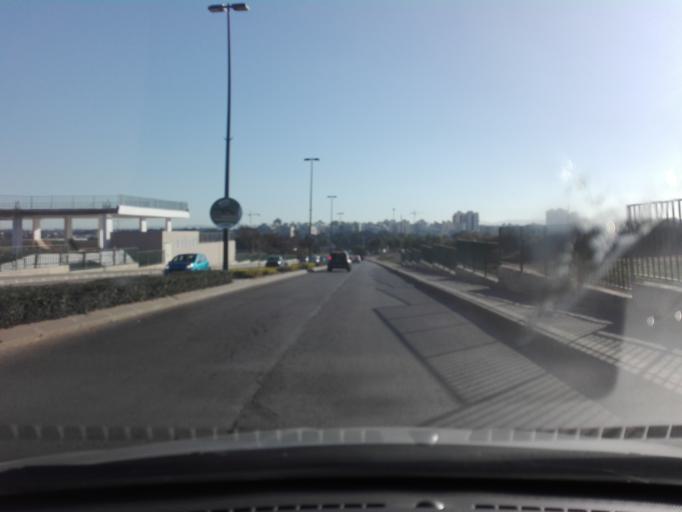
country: IL
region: Central District
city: Netanya
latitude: 32.3085
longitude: 34.8591
